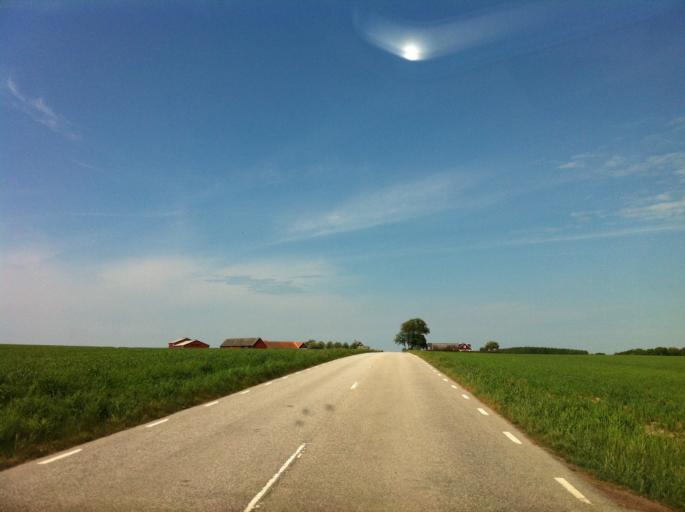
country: SE
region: Skane
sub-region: Helsingborg
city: Glumslov
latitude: 55.9198
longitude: 12.8609
